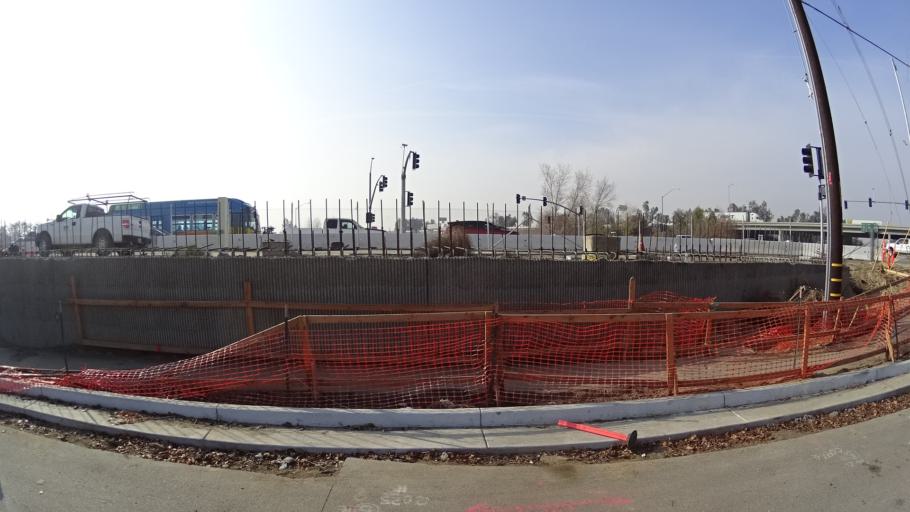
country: US
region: California
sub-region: Kern County
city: Bakersfield
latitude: 35.3832
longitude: -119.0428
